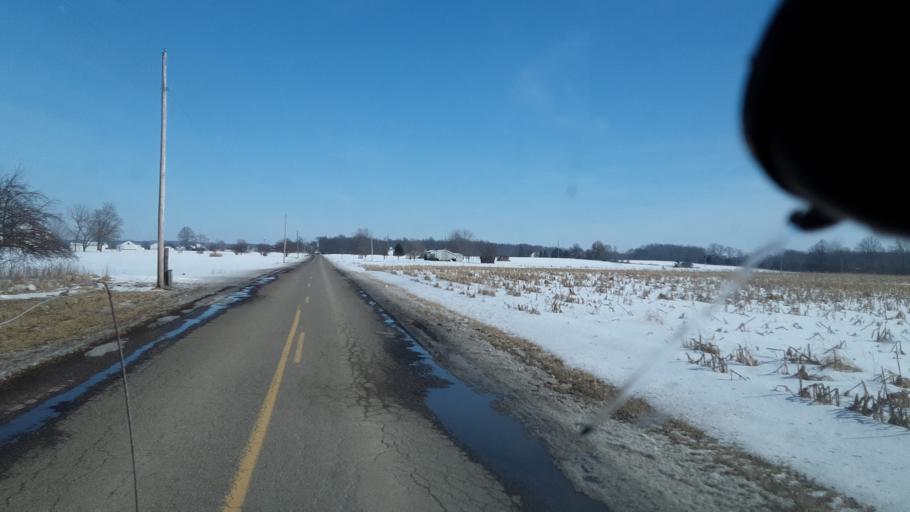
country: US
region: Ohio
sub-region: Mahoning County
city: Sebring
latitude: 40.9595
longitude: -80.9909
